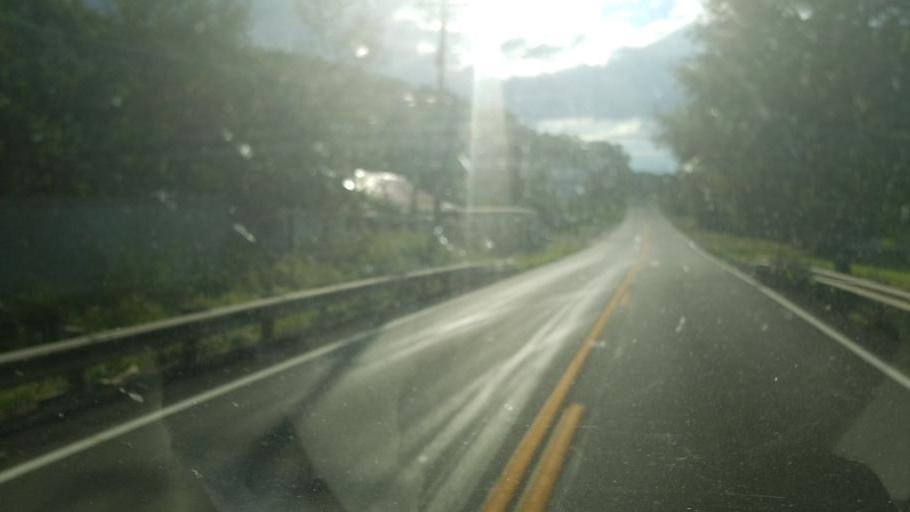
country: US
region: Ohio
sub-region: Knox County
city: Oak Hill
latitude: 40.4605
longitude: -82.0924
